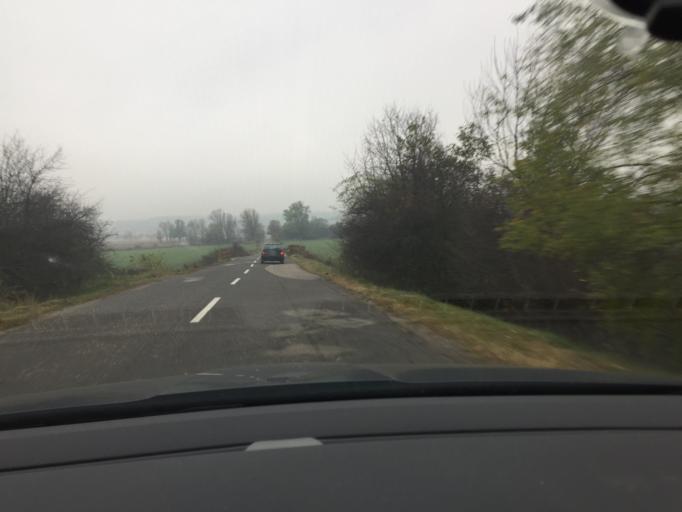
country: SK
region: Banskobystricky
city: Dudince
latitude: 48.1409
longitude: 18.8928
